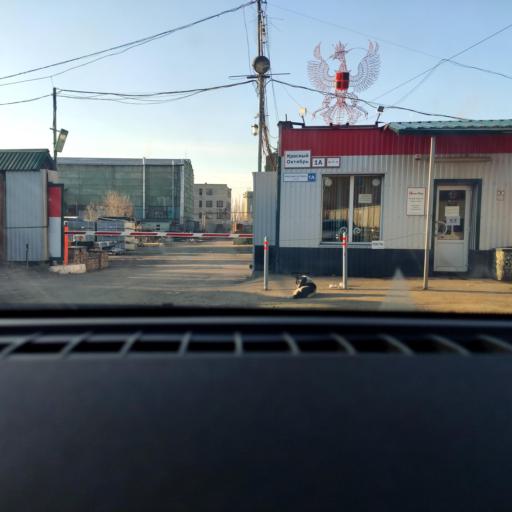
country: RU
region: Voronezj
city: Maslovka
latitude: 51.6292
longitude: 39.2575
